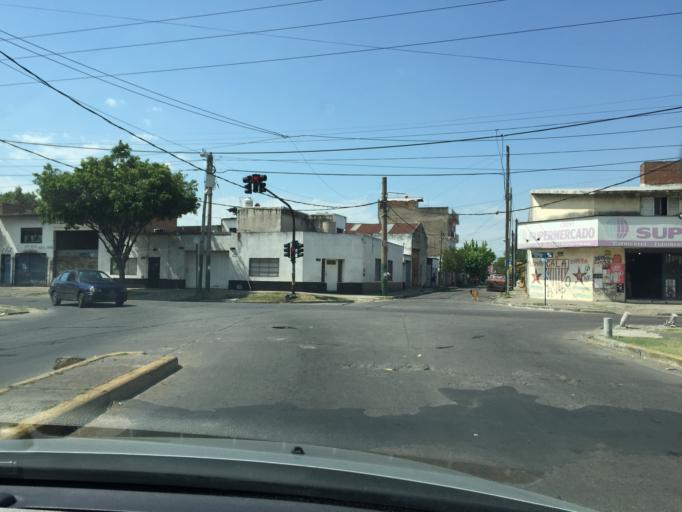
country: AR
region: Buenos Aires
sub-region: Partido de Lomas de Zamora
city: Lomas de Zamora
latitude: -34.7460
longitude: -58.4246
